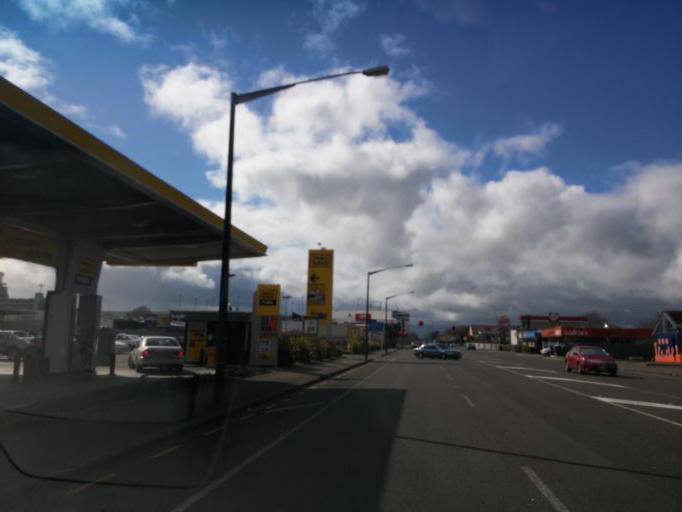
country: NZ
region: Manawatu-Wanganui
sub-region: Palmerston North City
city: Palmerston North
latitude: -40.3601
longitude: 175.6118
